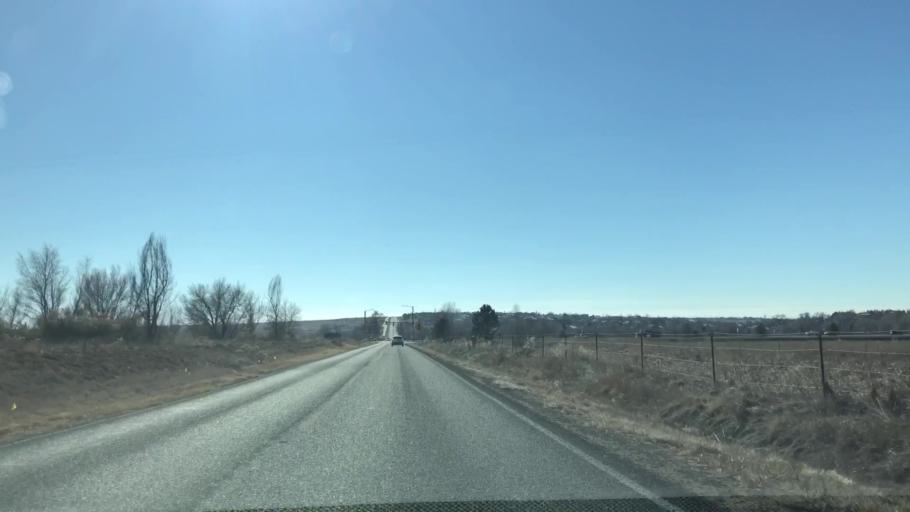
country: US
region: Colorado
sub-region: Weld County
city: Windsor
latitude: 40.4820
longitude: -104.9442
